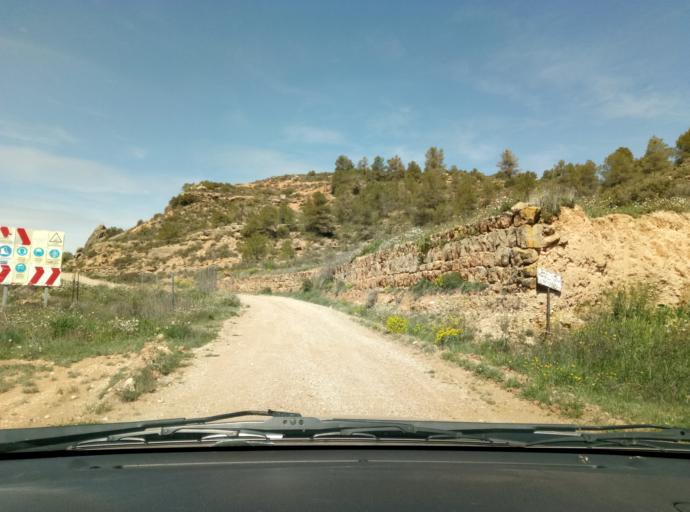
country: ES
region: Catalonia
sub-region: Provincia de Lleida
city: Juncosa
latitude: 41.4430
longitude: 0.8030
